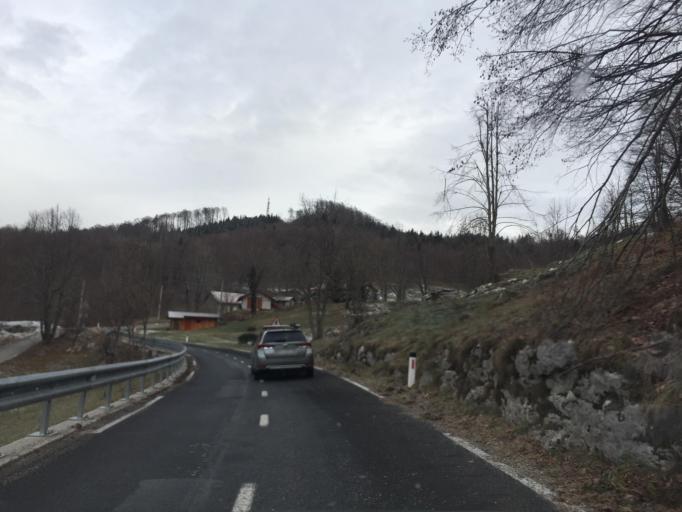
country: SI
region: Nova Gorica
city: Sempas
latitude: 46.0098
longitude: 13.7838
